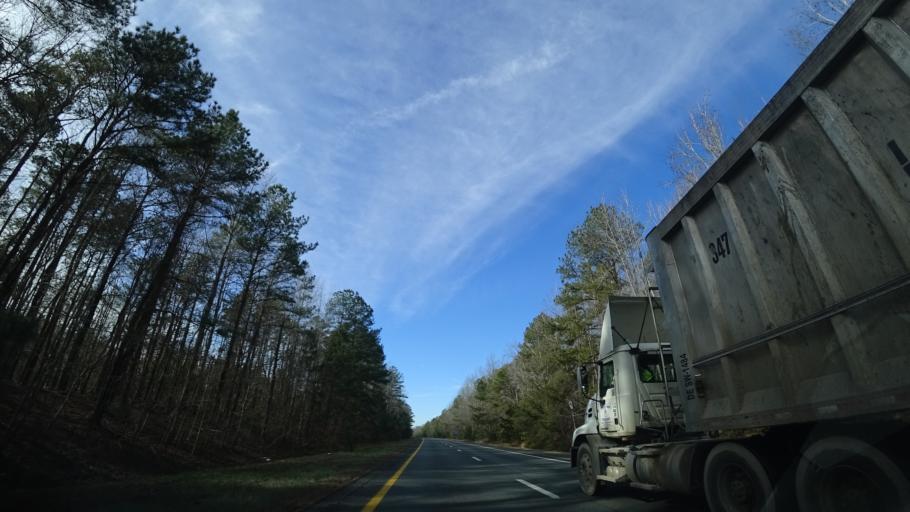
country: US
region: Virginia
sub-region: New Kent County
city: New Kent
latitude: 37.5064
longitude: -77.1022
